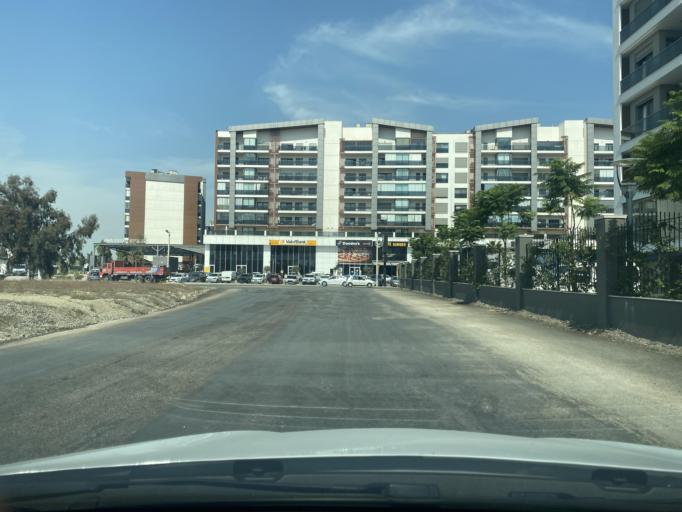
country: TR
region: Izmir
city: Karsiyaka
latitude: 38.4930
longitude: 27.0477
